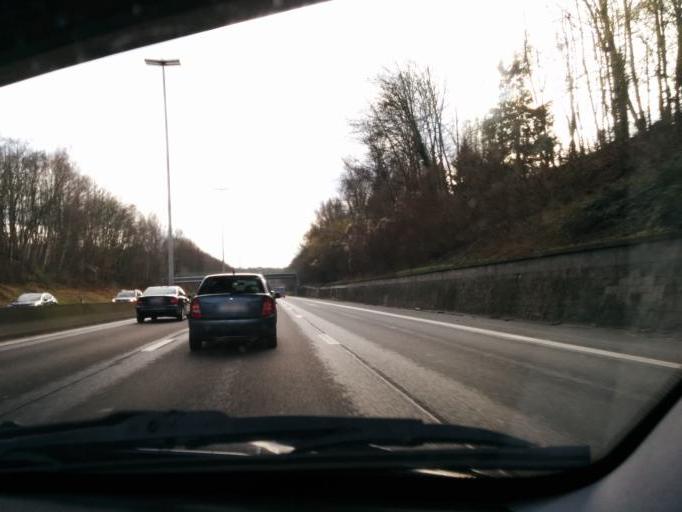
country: BE
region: Flanders
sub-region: Provincie Vlaams-Brabant
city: Wezembeek-Oppem
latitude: 50.8410
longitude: 4.4835
